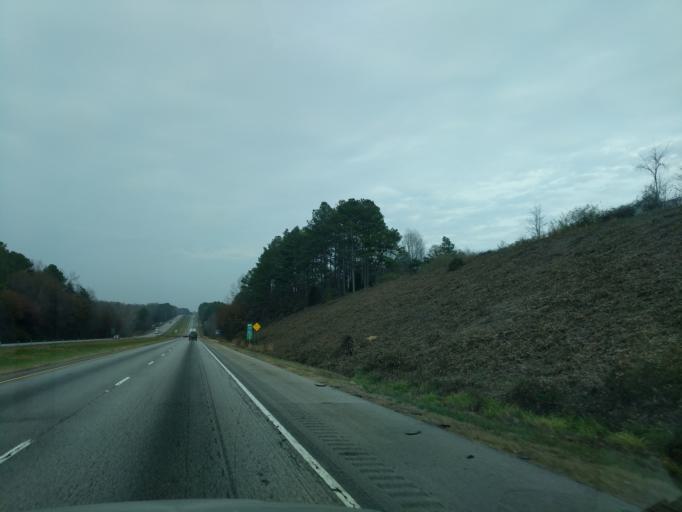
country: US
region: Georgia
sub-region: Franklin County
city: Carnesville
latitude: 34.3341
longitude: -83.3449
